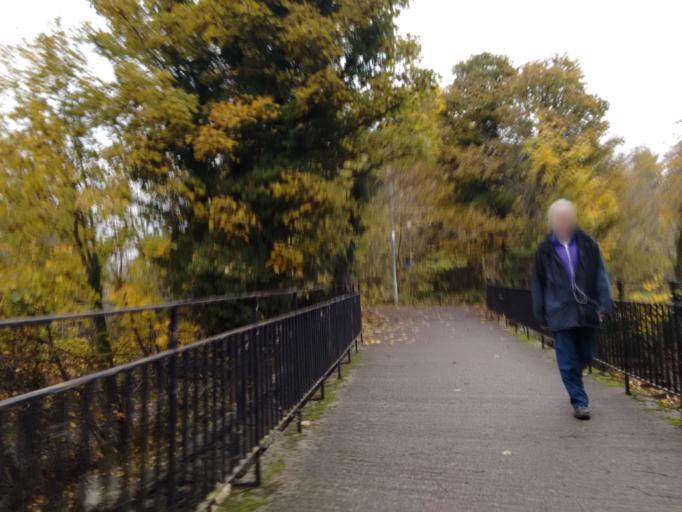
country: GB
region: Scotland
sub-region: Edinburgh
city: Colinton
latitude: 55.9201
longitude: -3.2569
